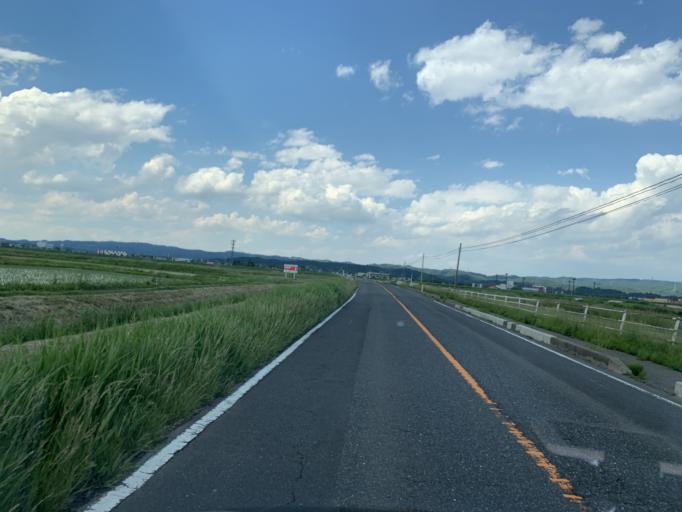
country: JP
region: Miyagi
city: Wakuya
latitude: 38.5241
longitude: 141.1304
